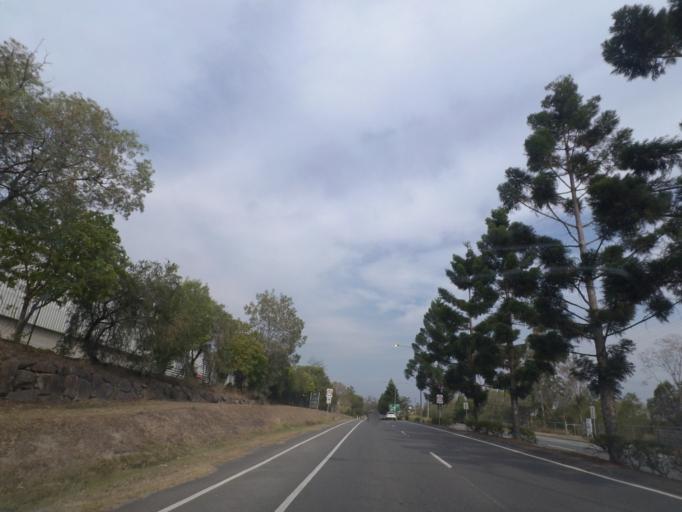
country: AU
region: Queensland
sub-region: Brisbane
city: Sunnybank
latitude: -27.5977
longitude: 153.0313
